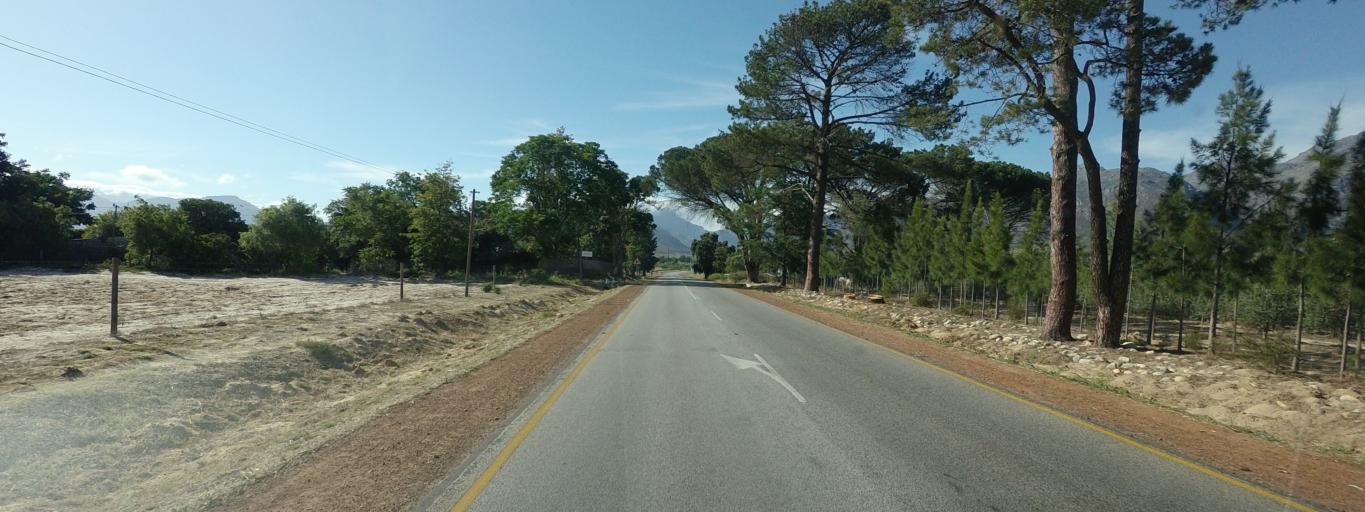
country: ZA
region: Western Cape
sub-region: Cape Winelands District Municipality
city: Paarl
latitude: -33.8699
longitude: 19.0430
